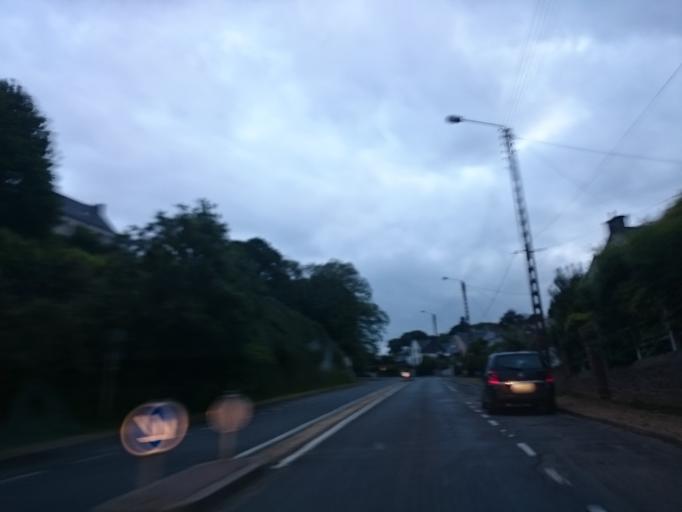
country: FR
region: Brittany
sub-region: Departement des Cotes-d'Armor
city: Perros-Guirec
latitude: 48.8125
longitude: -3.4617
